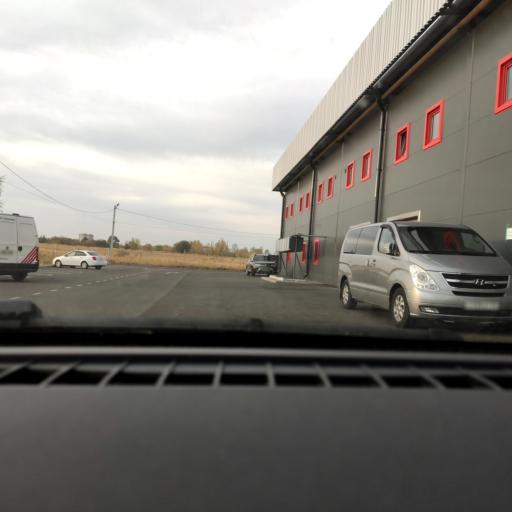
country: RU
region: Voronezj
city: Voronezh
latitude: 51.6785
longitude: 39.2823
